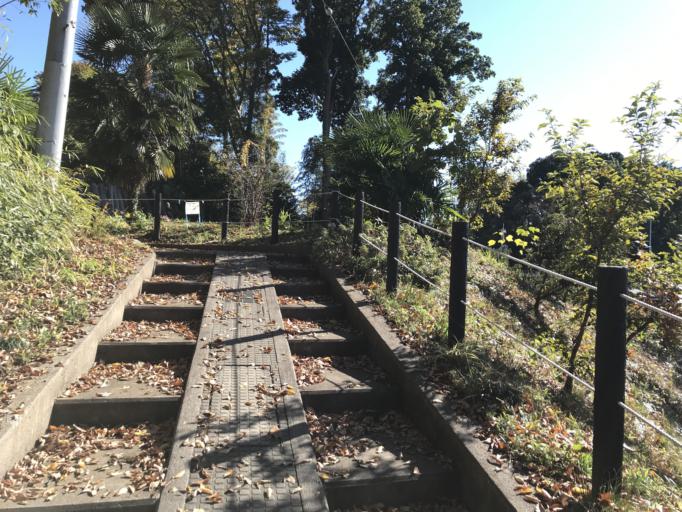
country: JP
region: Chiba
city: Nagareyama
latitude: 35.8441
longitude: 139.9087
